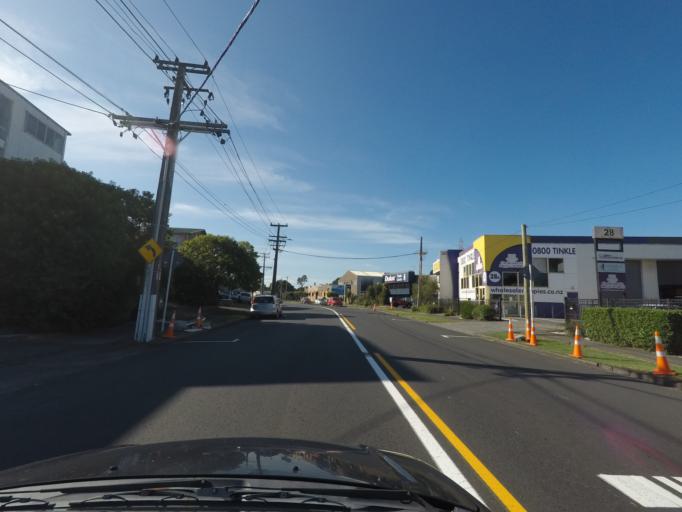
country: NZ
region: Auckland
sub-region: Auckland
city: Waitakere
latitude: -36.9068
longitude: 174.6906
